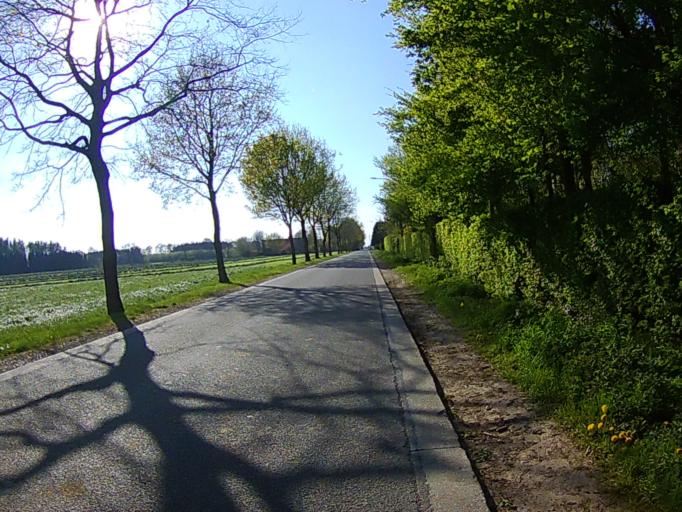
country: BE
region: Flanders
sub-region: Provincie Antwerpen
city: Hoogstraten
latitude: 51.3827
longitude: 4.7391
